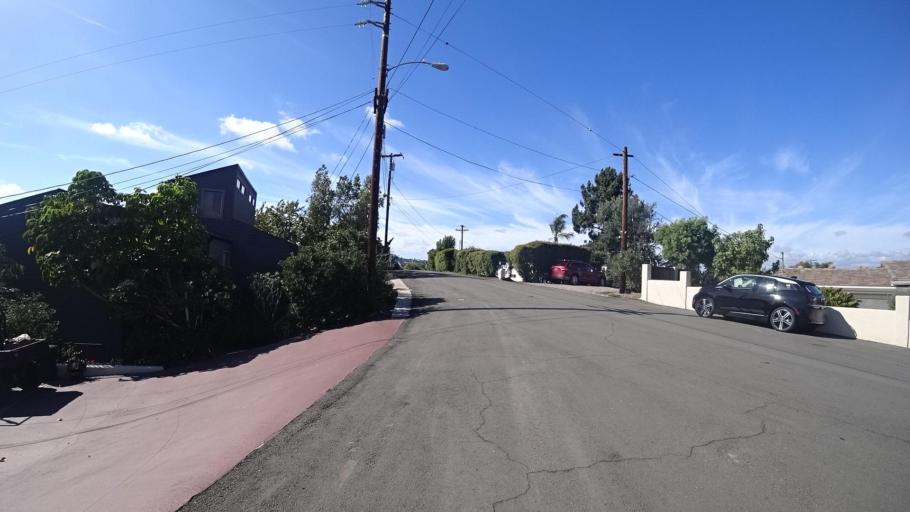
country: US
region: California
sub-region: San Diego County
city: Casa de Oro-Mount Helix
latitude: 32.7595
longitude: -116.9575
